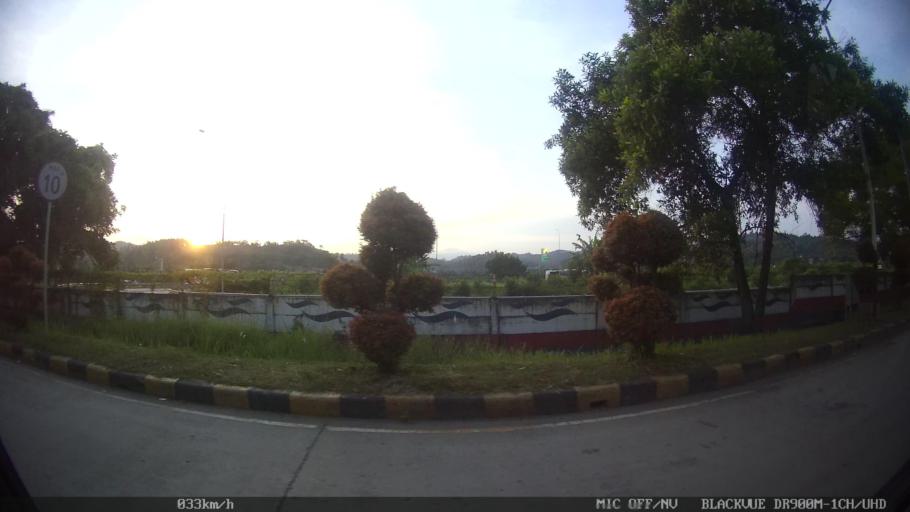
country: ID
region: Lampung
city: Penengahan
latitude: -5.8717
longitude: 105.7509
